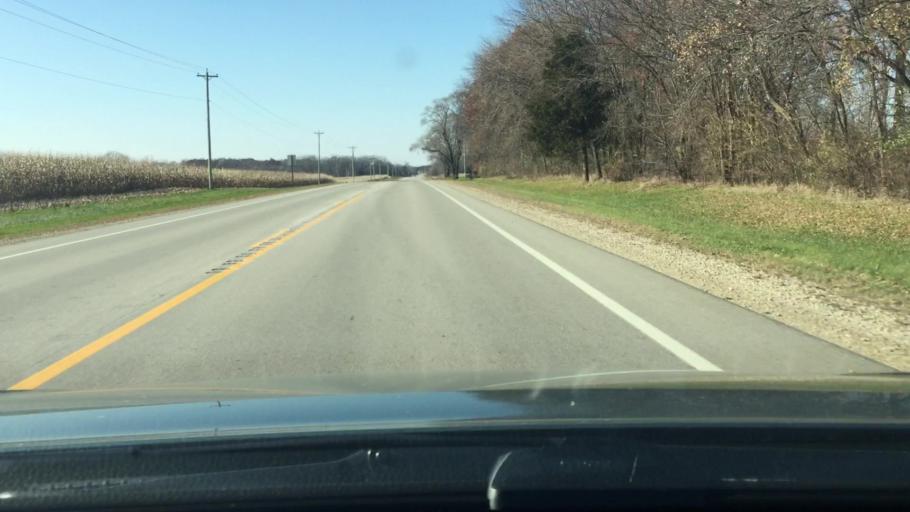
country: US
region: Wisconsin
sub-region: Jefferson County
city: Lake Ripley
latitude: 43.0076
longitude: -88.9250
